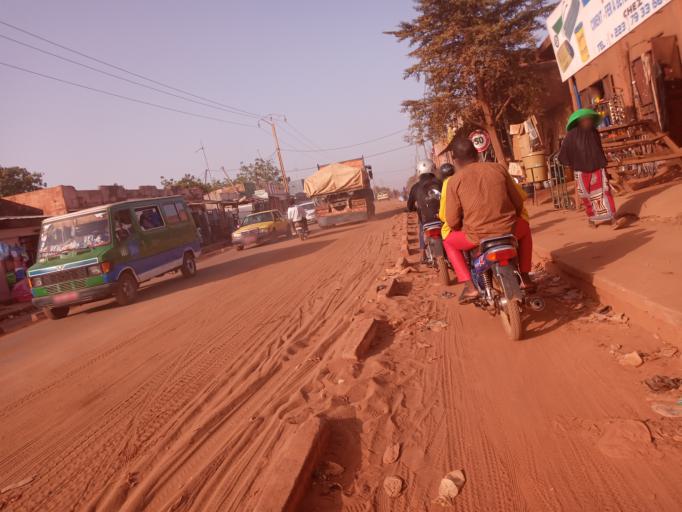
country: ML
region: Bamako
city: Bamako
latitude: 12.5777
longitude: -8.0260
